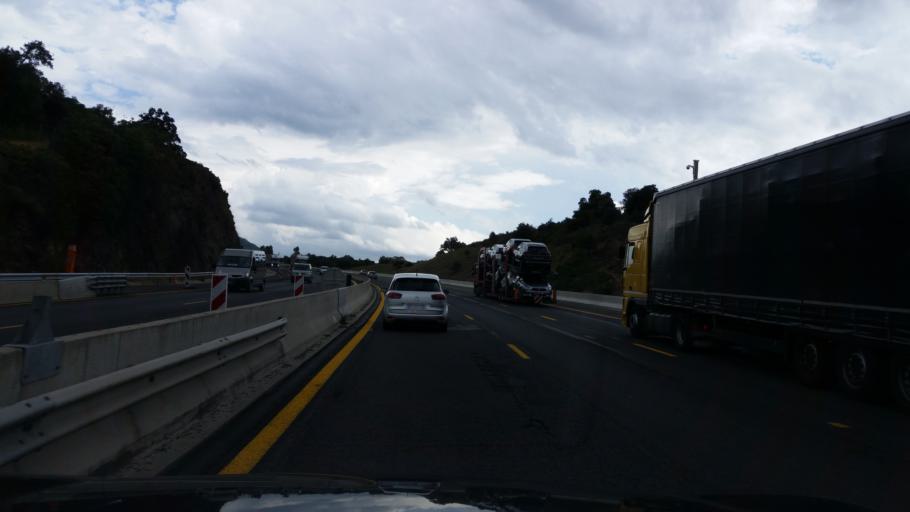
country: FR
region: Languedoc-Roussillon
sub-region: Departement des Pyrenees-Orientales
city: Maureillas-las-Illas
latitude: 42.4814
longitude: 2.8454
